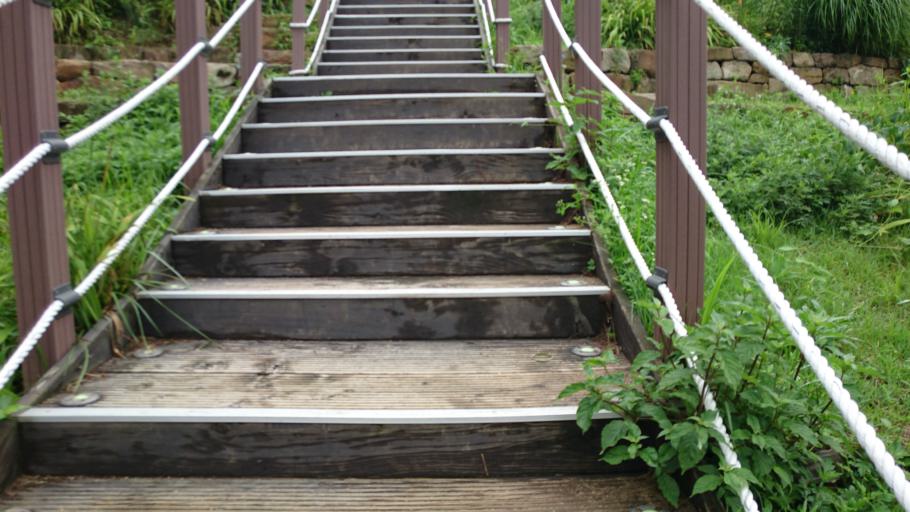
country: KR
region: Gyeonggi-do
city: Suwon-si
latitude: 37.2804
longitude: 127.0107
